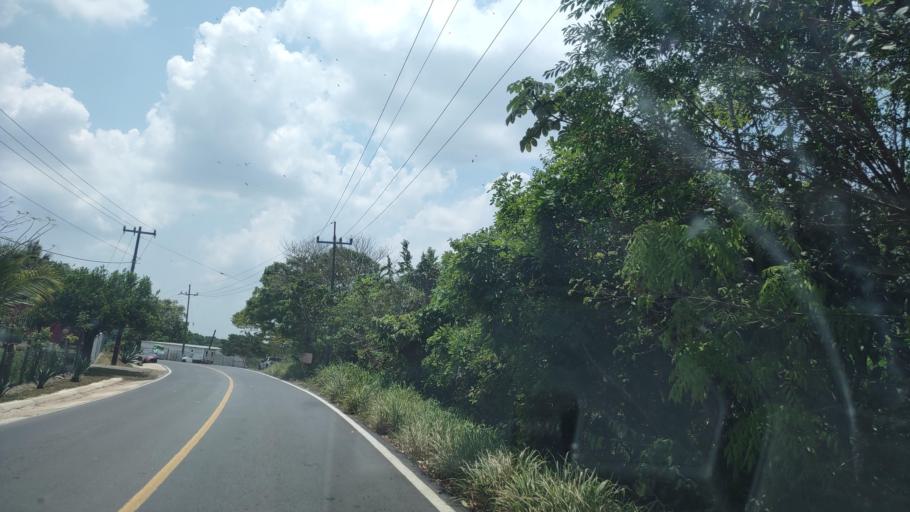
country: MX
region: Veracruz
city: Las Choapas
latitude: 17.9285
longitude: -94.1481
